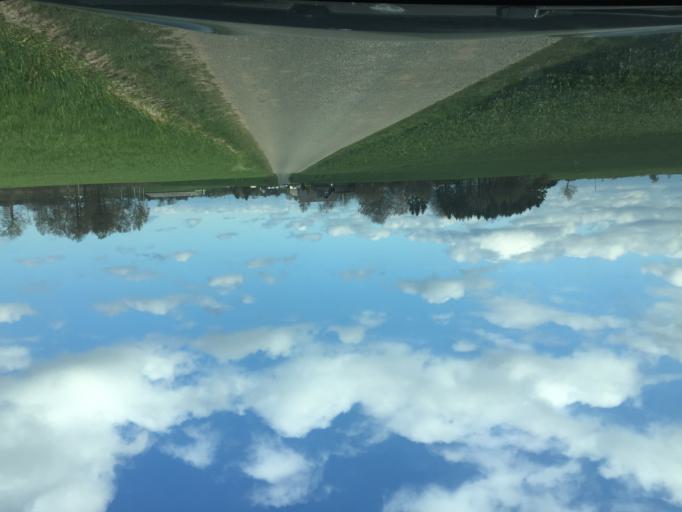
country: DK
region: South Denmark
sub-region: Faaborg-Midtfyn Kommune
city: Arslev
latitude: 55.3261
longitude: 10.4598
